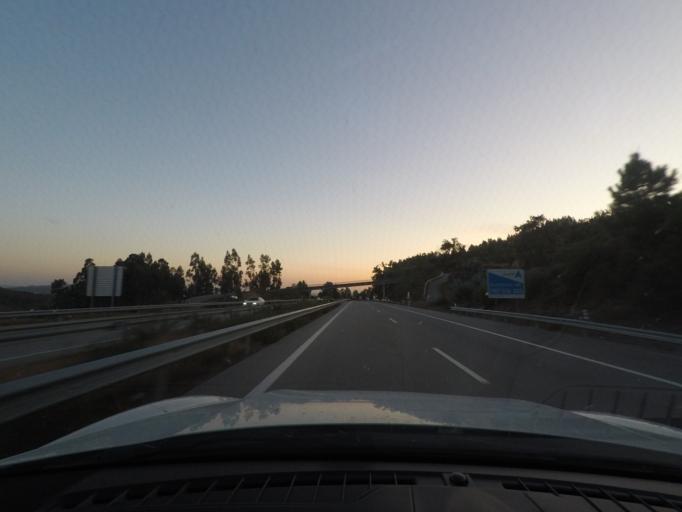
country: PT
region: Porto
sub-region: Lousada
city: Lousada
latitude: 41.3191
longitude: -8.2425
